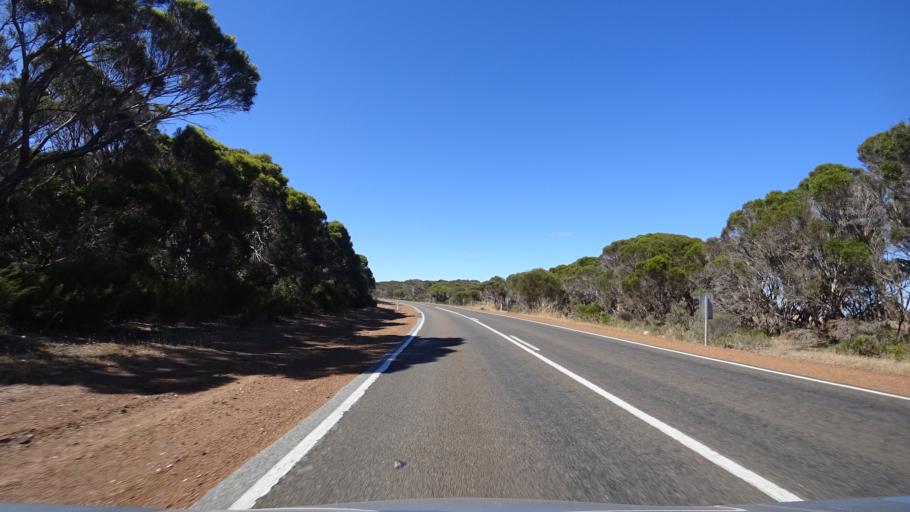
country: AU
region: South Australia
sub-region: Kangaroo Island
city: Kingscote
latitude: -35.7172
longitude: 137.5601
